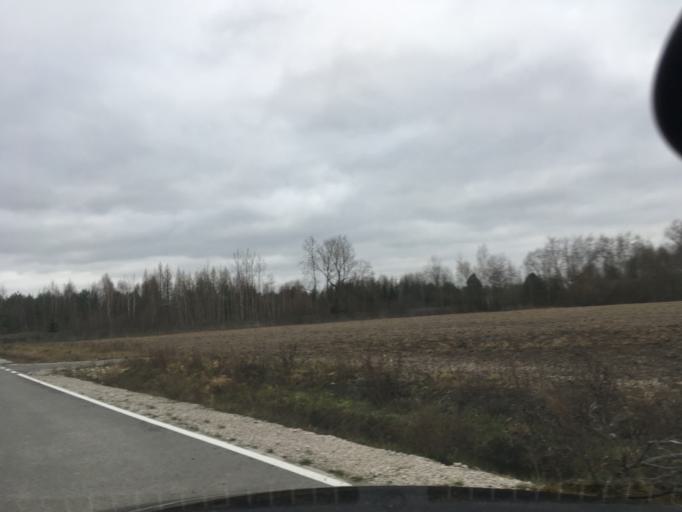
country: PL
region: Masovian Voivodeship
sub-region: Powiat piaseczynski
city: Lesznowola
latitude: 52.0476
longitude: 20.9245
